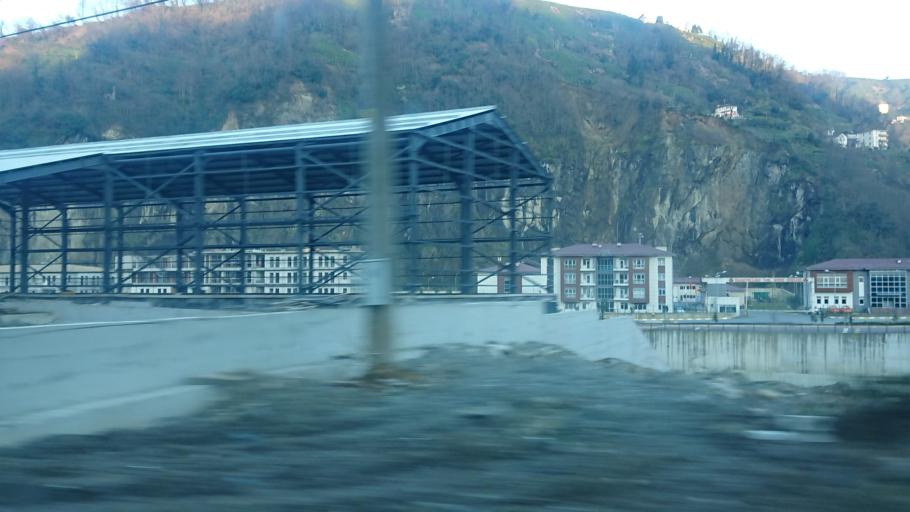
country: TR
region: Rize
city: Gundogdu
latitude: 41.0282
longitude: 40.5812
